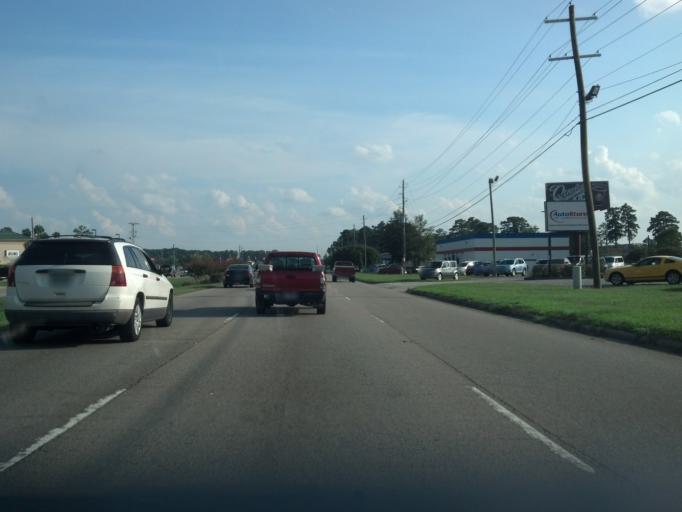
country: US
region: North Carolina
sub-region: Pitt County
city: Summerfield
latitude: 35.5553
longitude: -77.4063
